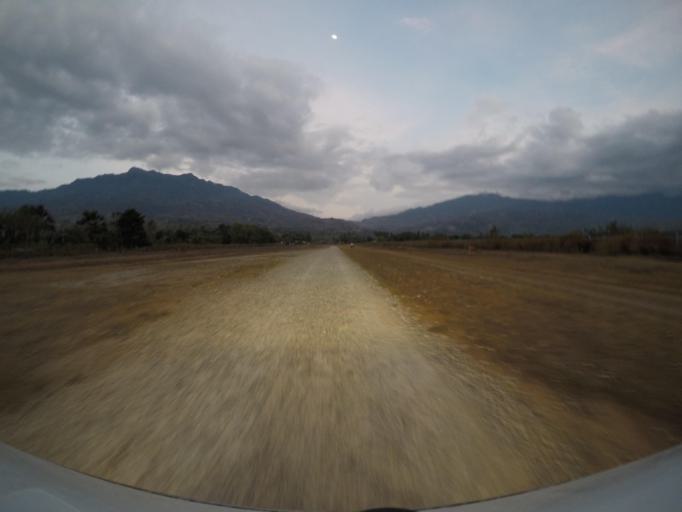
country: TL
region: Bobonaro
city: Maliana
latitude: -8.9728
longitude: 125.2161
